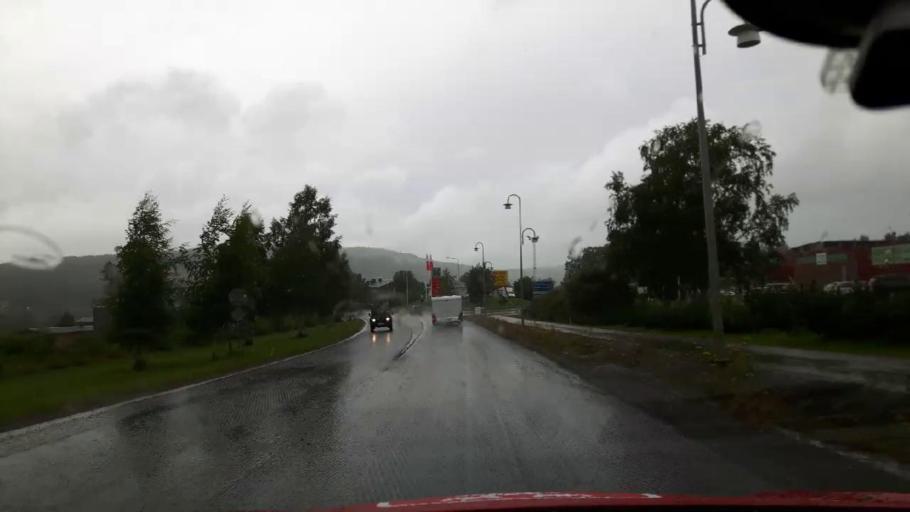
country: SE
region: Jaemtland
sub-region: Are Kommun
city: Jarpen
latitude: 63.3451
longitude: 13.4648
